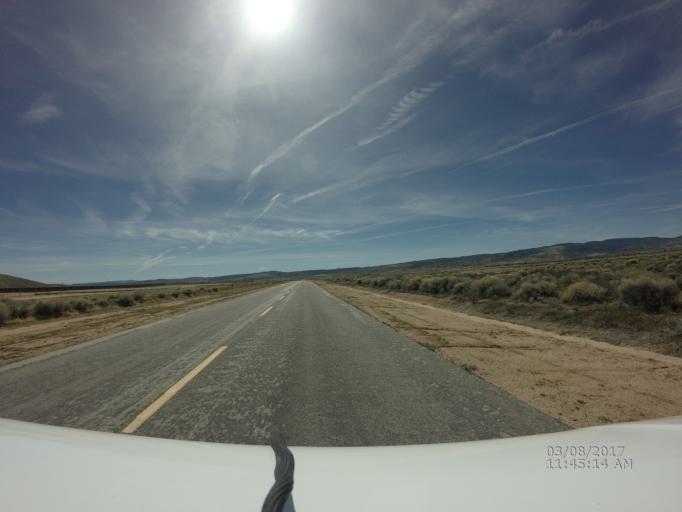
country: US
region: California
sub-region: Los Angeles County
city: Green Valley
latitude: 34.7633
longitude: -118.4311
